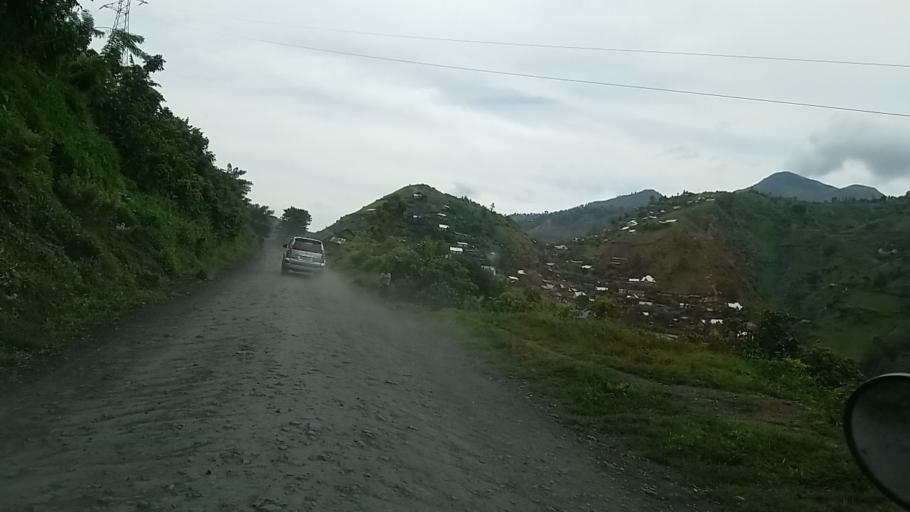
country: CD
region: Nord Kivu
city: Sake
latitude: -1.7532
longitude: 28.9862
